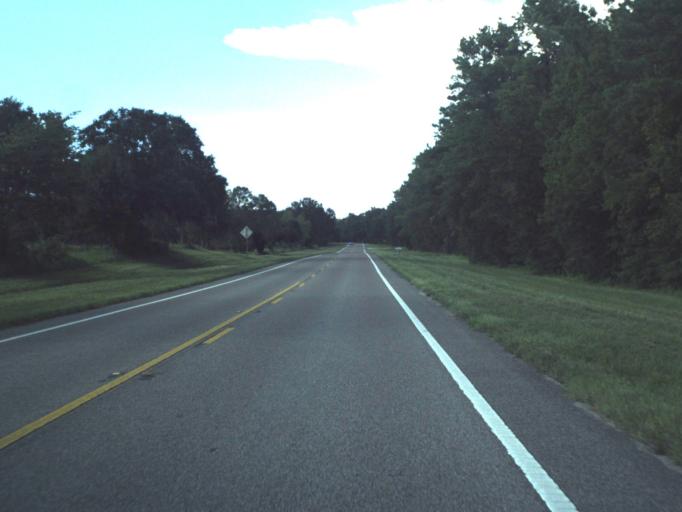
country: US
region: Florida
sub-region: Hernando County
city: North Brooksville
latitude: 28.5985
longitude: -82.4007
